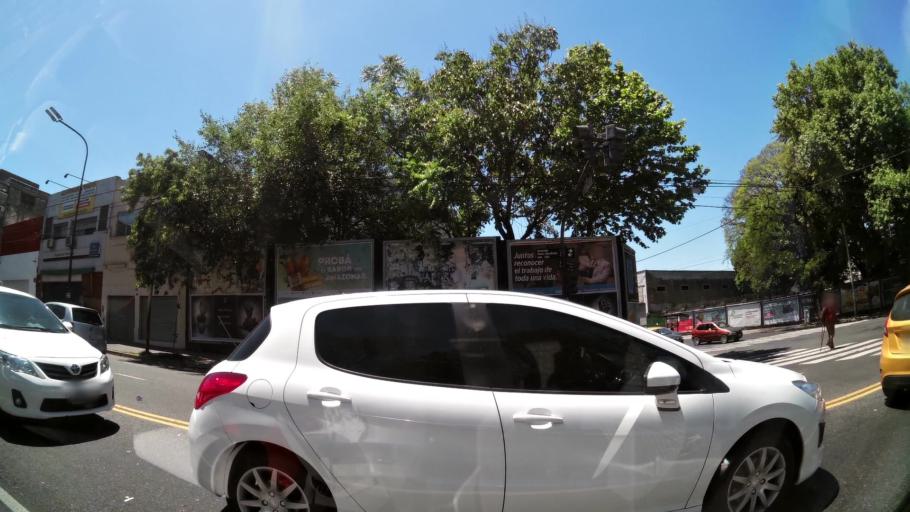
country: AR
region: Buenos Aires F.D.
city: Buenos Aires
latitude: -34.6400
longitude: -58.3899
